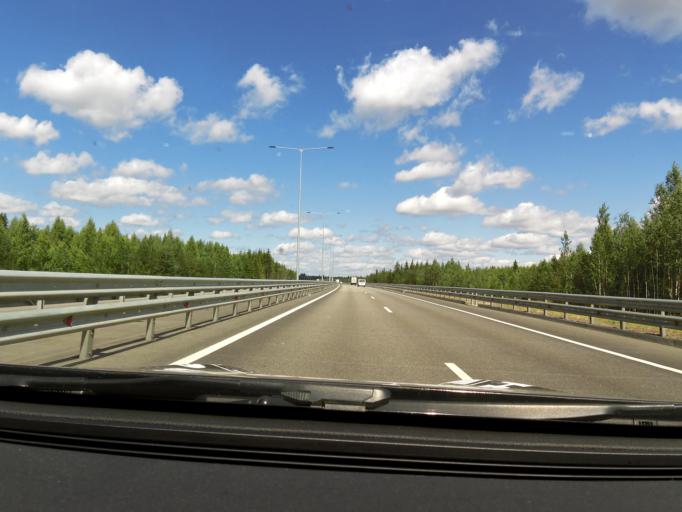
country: RU
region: Tverskaya
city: Krasnomayskiy
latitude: 57.6644
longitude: 34.2322
